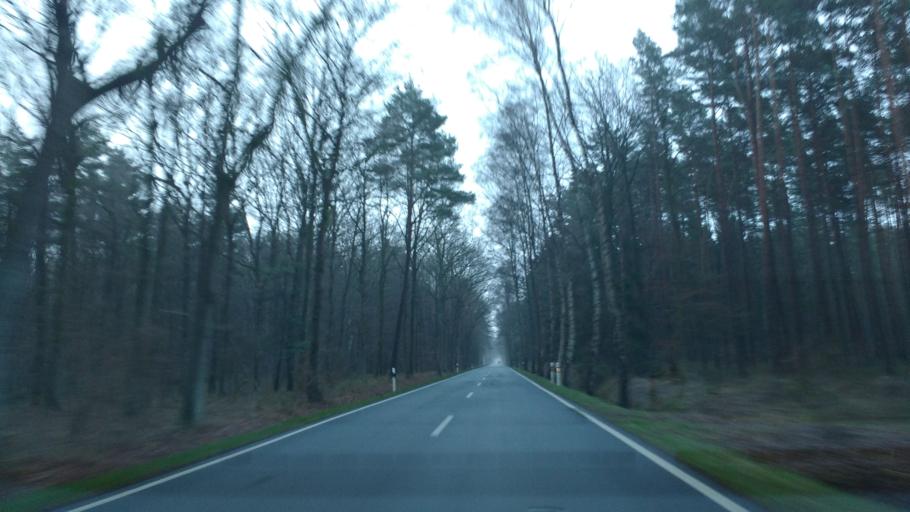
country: DE
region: Lower Saxony
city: Gilten
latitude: 52.6412
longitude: 9.5392
